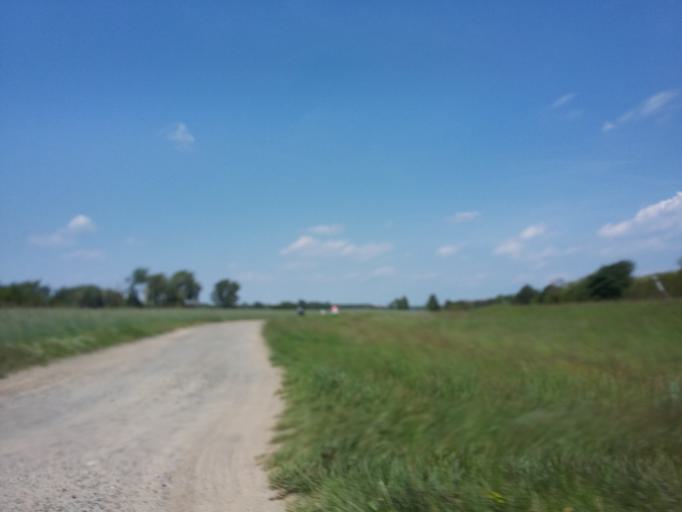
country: AT
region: Lower Austria
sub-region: Politischer Bezirk Ganserndorf
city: Drosing
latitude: 48.5084
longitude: 16.9558
